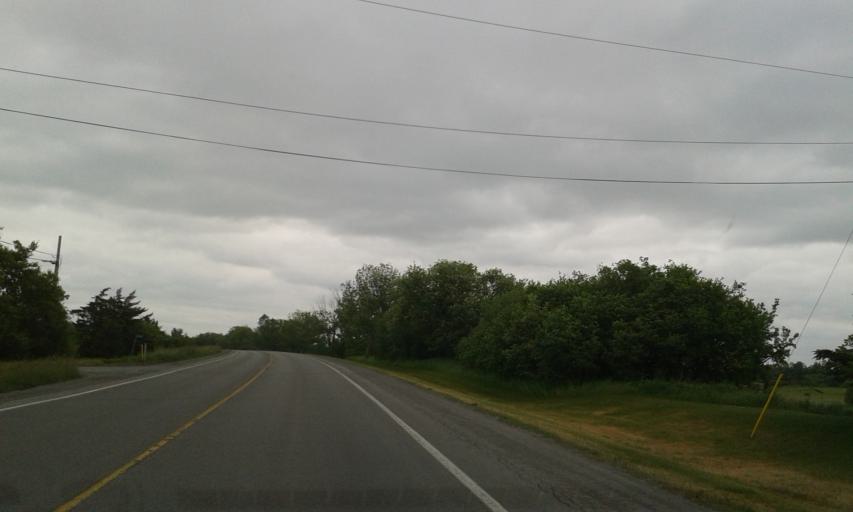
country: CA
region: Ontario
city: Prince Edward
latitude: 43.9608
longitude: -77.2957
